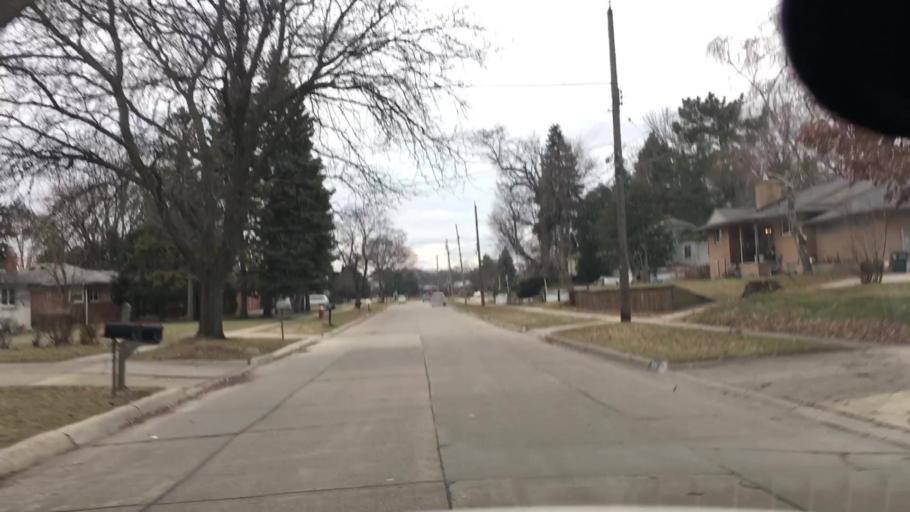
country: US
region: Michigan
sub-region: Oakland County
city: Madison Heights
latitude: 42.5007
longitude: -83.0737
